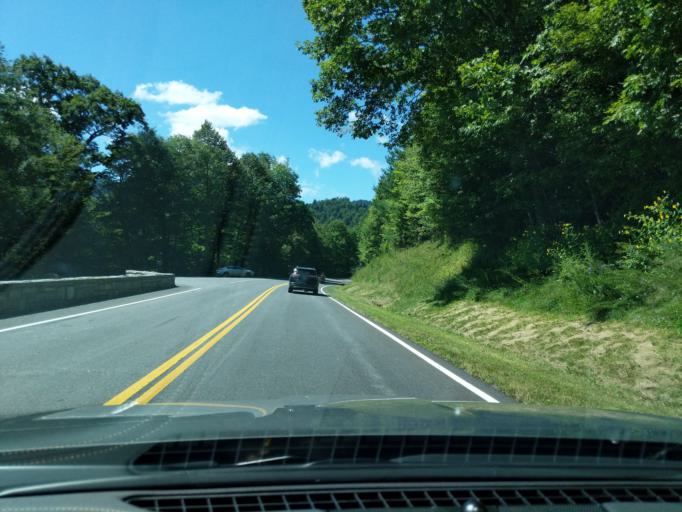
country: US
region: Tennessee
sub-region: Sevier County
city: Gatlinburg
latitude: 35.5979
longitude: -83.4205
